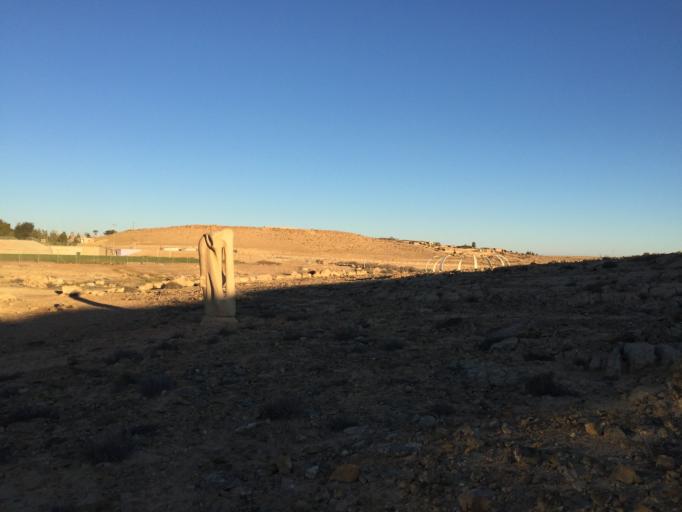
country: IL
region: Southern District
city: Mitzpe Ramon
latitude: 30.6131
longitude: 34.8077
